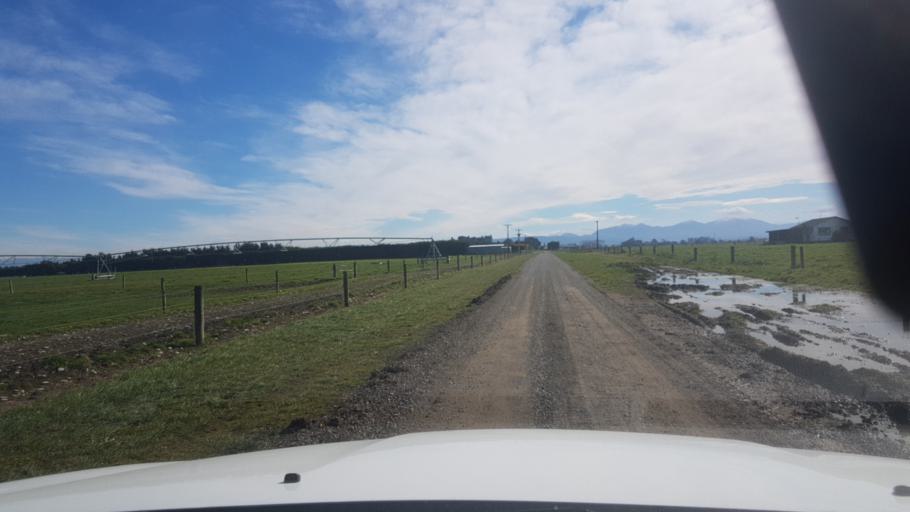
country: NZ
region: Canterbury
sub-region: Timaru District
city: Timaru
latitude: -44.2511
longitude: 171.3881
